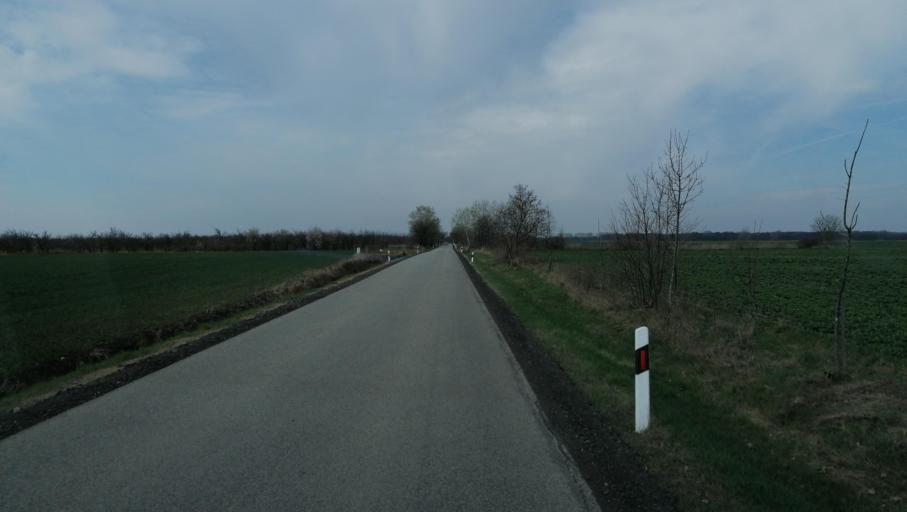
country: HU
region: Pest
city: Kiskunlachaza
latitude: 47.1908
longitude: 18.9938
